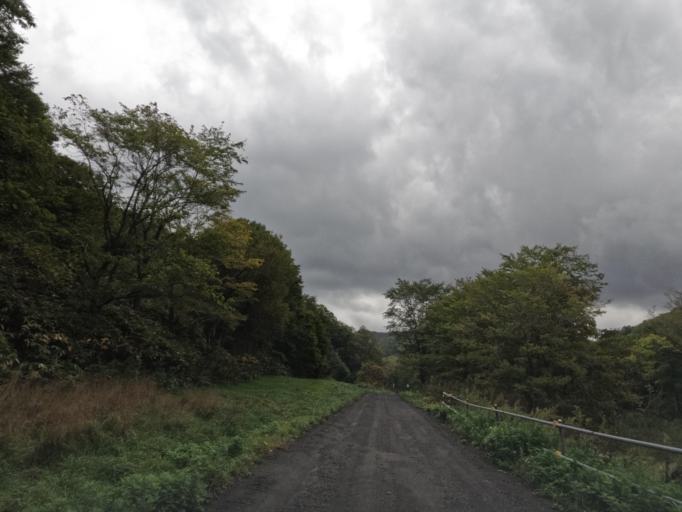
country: JP
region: Hokkaido
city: Date
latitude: 42.5006
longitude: 140.9123
